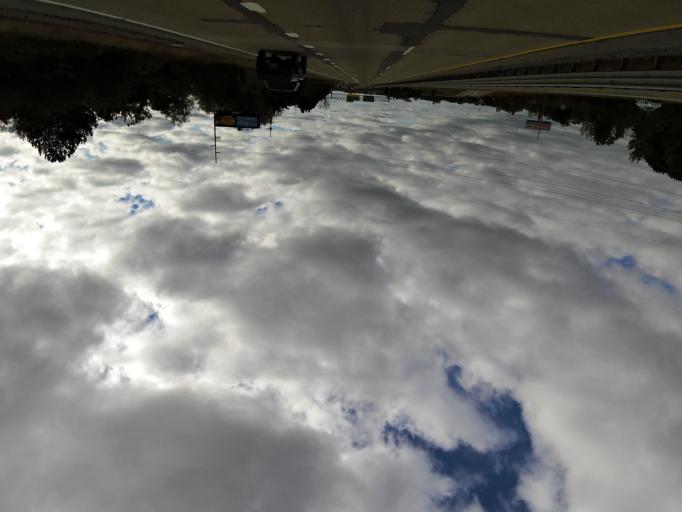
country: US
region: Michigan
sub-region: Genesee County
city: Flint
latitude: 42.9812
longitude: -83.7451
